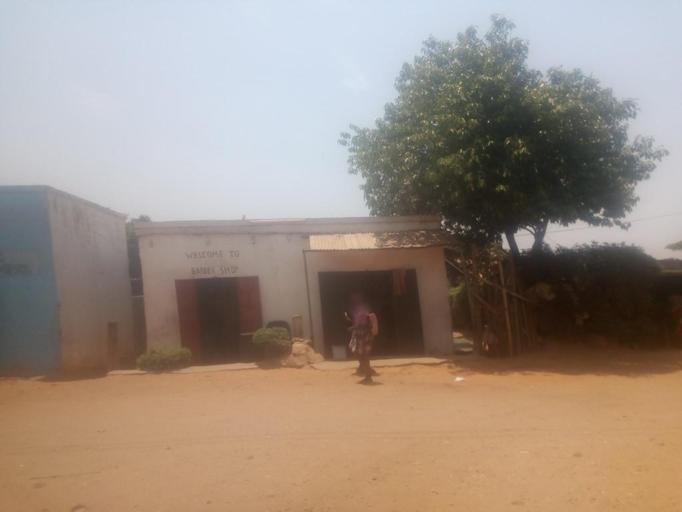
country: ZM
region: Lusaka
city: Lusaka
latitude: -15.4045
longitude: 28.3721
